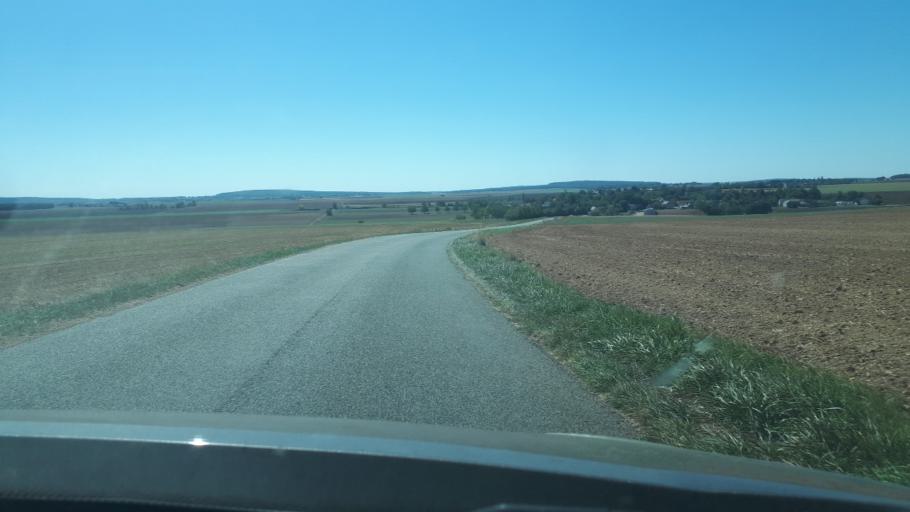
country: FR
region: Centre
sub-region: Departement du Cher
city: Baugy
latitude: 47.2162
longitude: 2.7498
